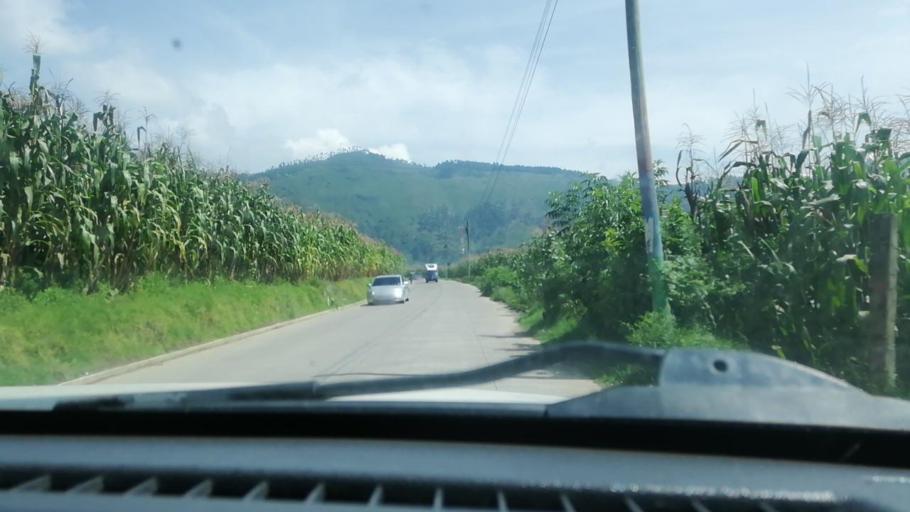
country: GT
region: Totonicapan
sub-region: Municipio de San Andres Xecul
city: San Andres Xecul
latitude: 14.8959
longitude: -91.4778
